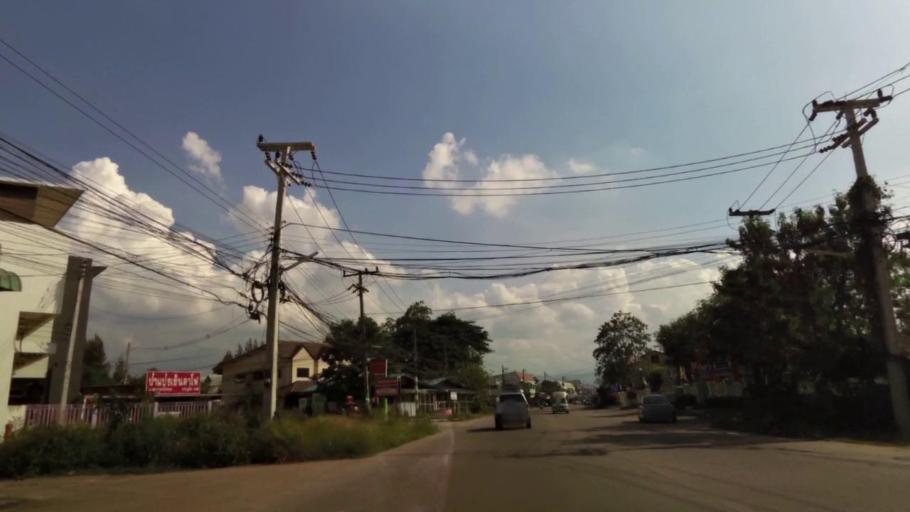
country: TH
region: Phrae
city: Phrae
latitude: 18.1242
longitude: 100.1522
